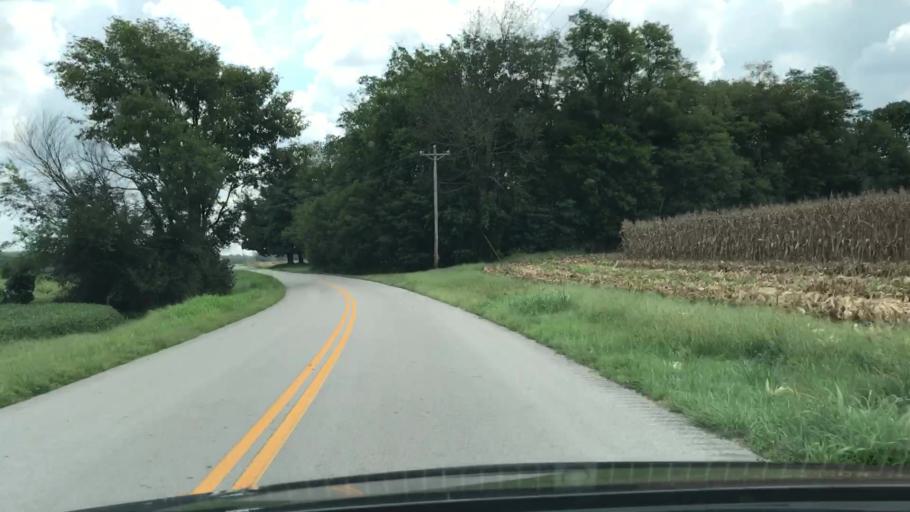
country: US
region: Kentucky
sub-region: Todd County
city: Elkton
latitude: 36.7717
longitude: -87.1170
